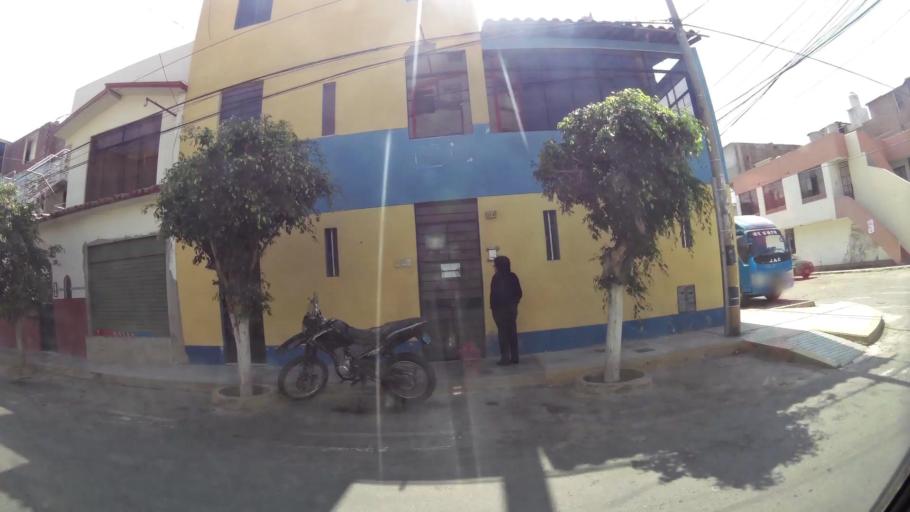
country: PE
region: La Libertad
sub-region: Provincia de Trujillo
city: Buenos Aires
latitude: -8.1258
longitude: -79.0431
